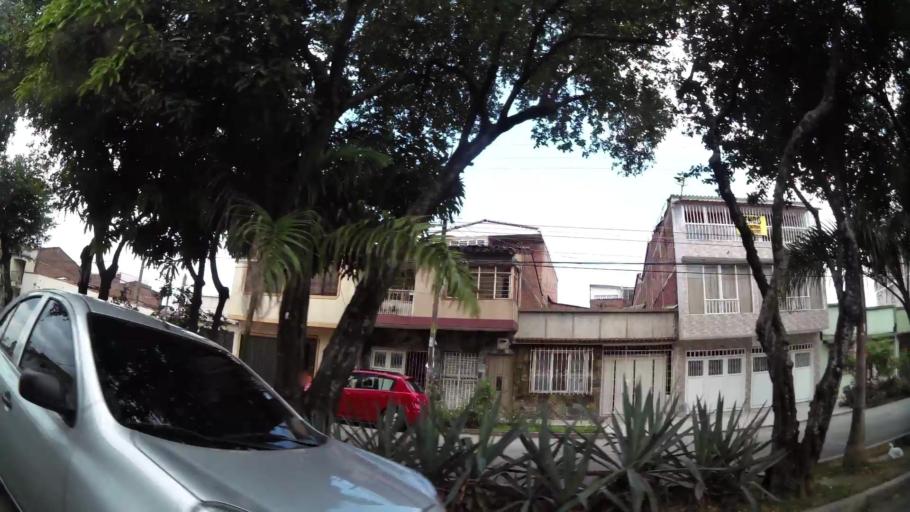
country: CO
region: Valle del Cauca
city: Cali
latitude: 3.4379
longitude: -76.5305
